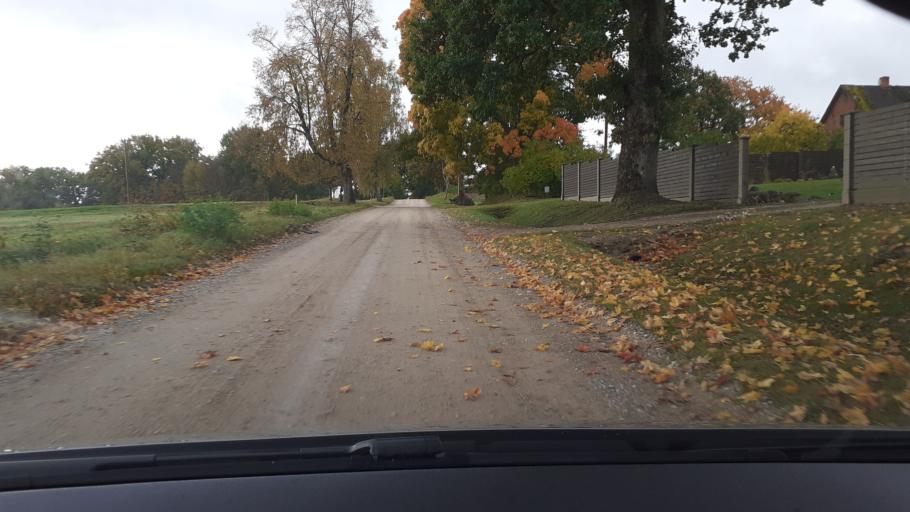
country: LV
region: Kuldigas Rajons
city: Kuldiga
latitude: 57.0272
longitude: 21.9149
